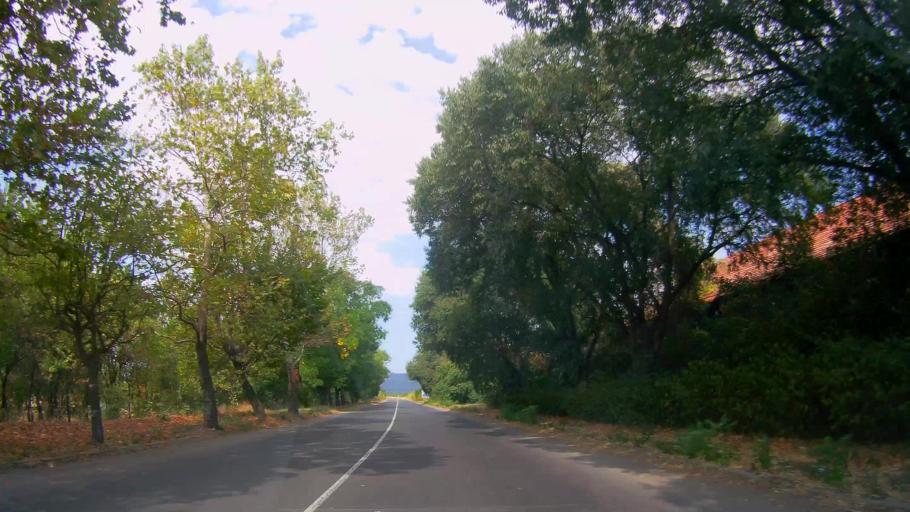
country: BG
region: Burgas
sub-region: Obshtina Aytos
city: Aytos
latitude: 42.7023
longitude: 27.2460
